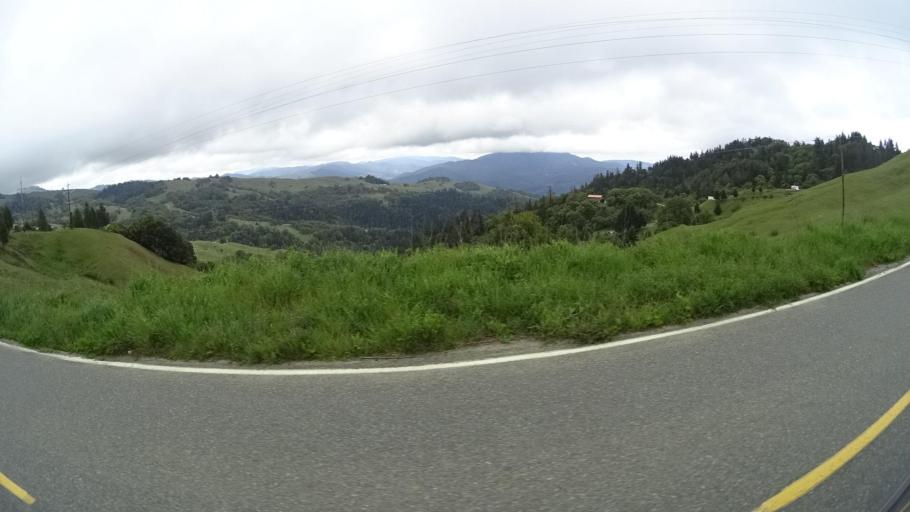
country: US
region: California
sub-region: Humboldt County
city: Redway
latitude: 40.1112
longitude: -123.7426
